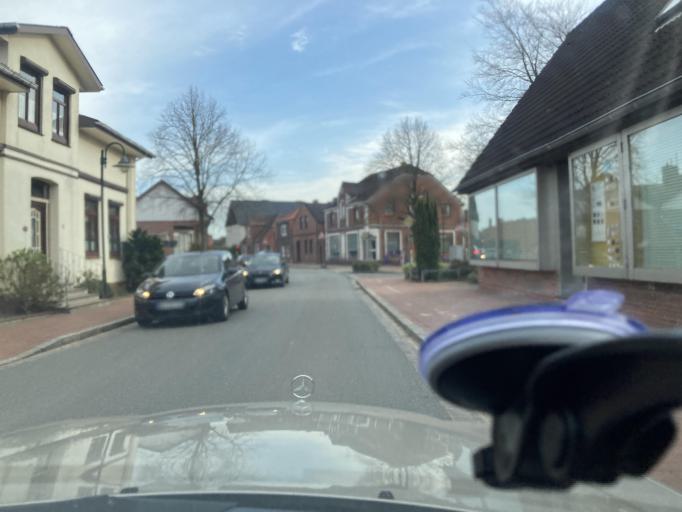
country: DE
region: Schleswig-Holstein
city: Lehe
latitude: 54.3305
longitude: 9.0221
